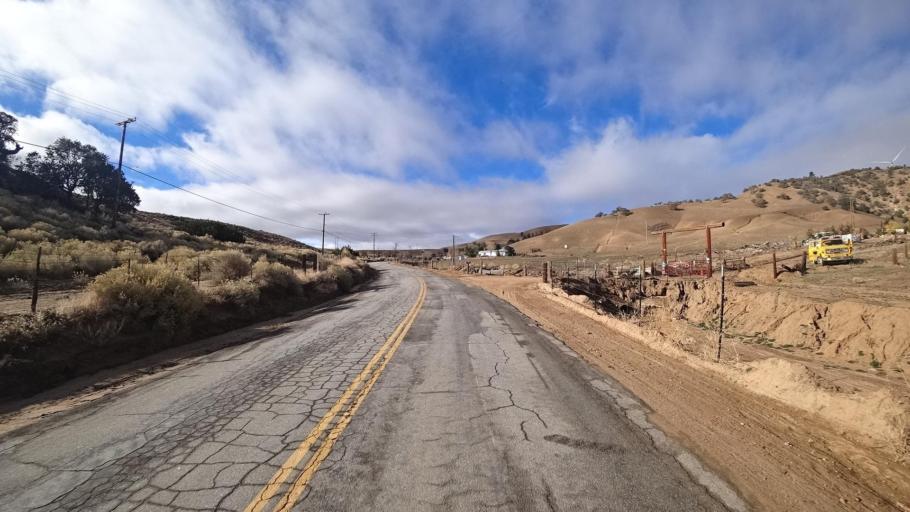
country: US
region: California
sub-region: Kern County
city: Tehachapi
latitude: 35.0761
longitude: -118.3392
